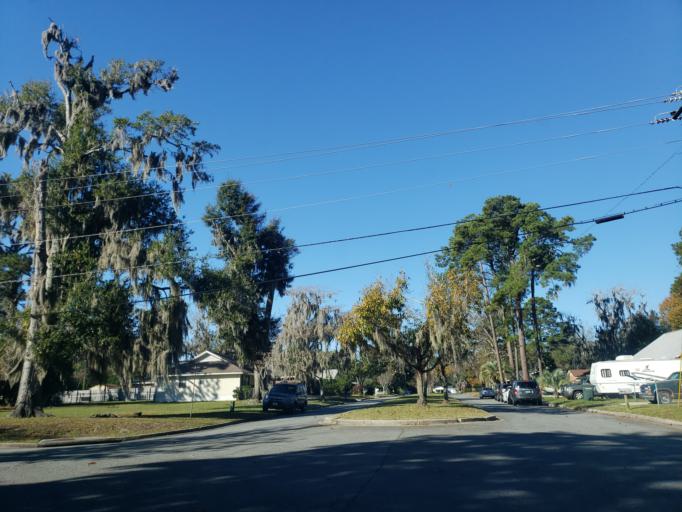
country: US
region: Georgia
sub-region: Chatham County
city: Isle of Hope
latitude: 31.9957
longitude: -81.1026
